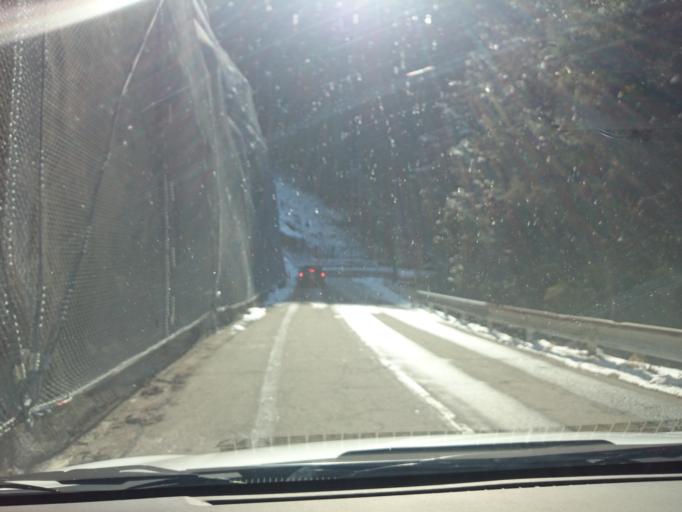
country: JP
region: Gifu
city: Gujo
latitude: 35.7469
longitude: 136.9756
